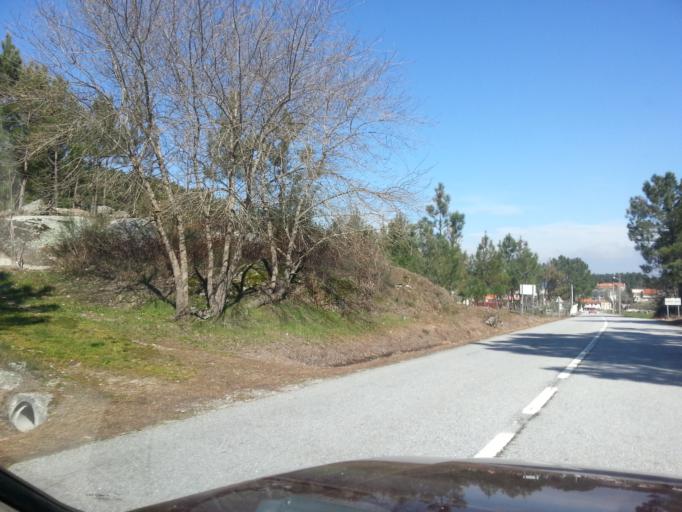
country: PT
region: Guarda
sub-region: Fornos de Algodres
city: Fornos de Algodres
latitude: 40.6440
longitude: -7.5315
